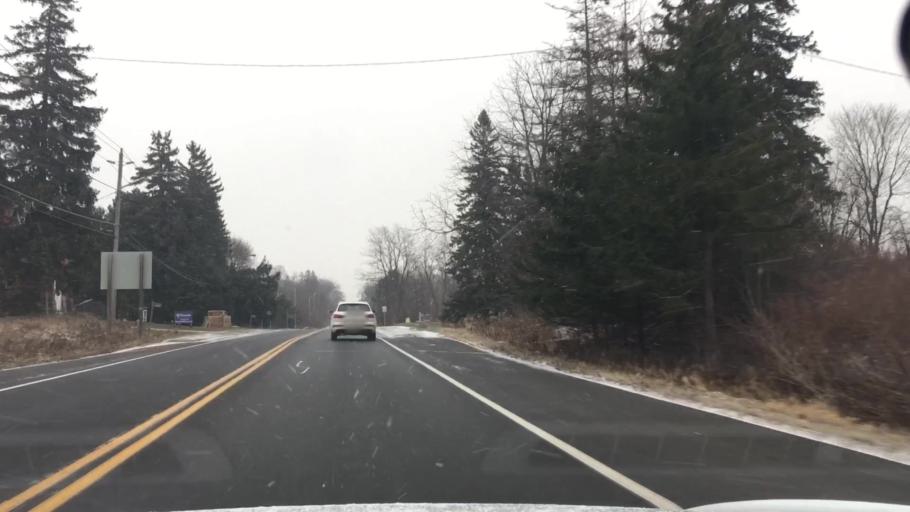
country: CA
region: Ontario
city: Markham
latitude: 43.8852
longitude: -79.2059
